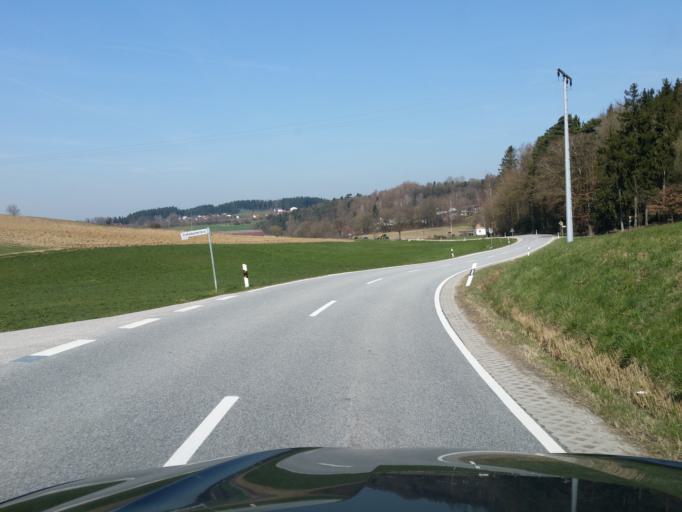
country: DE
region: Bavaria
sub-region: Upper Bavaria
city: Kirchberg
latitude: 48.4460
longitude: 12.0505
